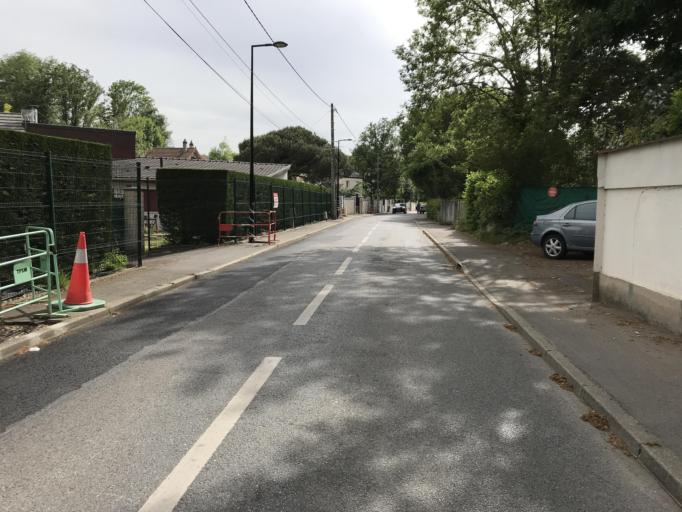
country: FR
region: Ile-de-France
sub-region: Departement de l'Essonne
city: La Ville-du-Bois
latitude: 48.6532
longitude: 2.2546
